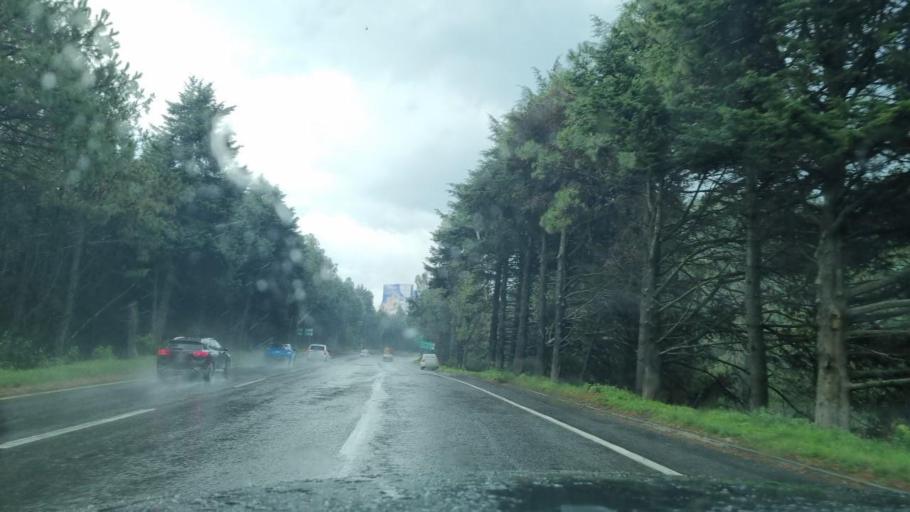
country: MX
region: Morelos
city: San Jeronimo Acazulco
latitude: 19.2964
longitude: -99.3969
